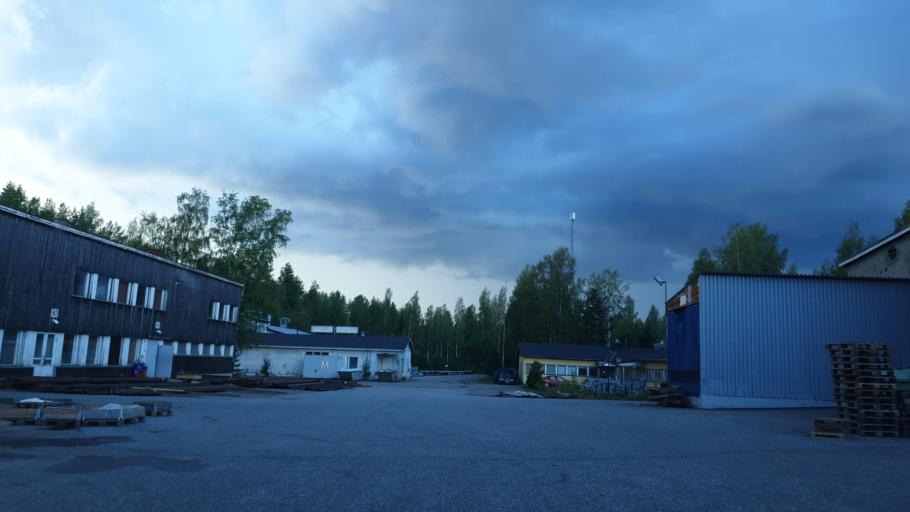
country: FI
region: Northern Savo
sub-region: Varkaus
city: Leppaevirta
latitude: 62.5803
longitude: 27.6087
